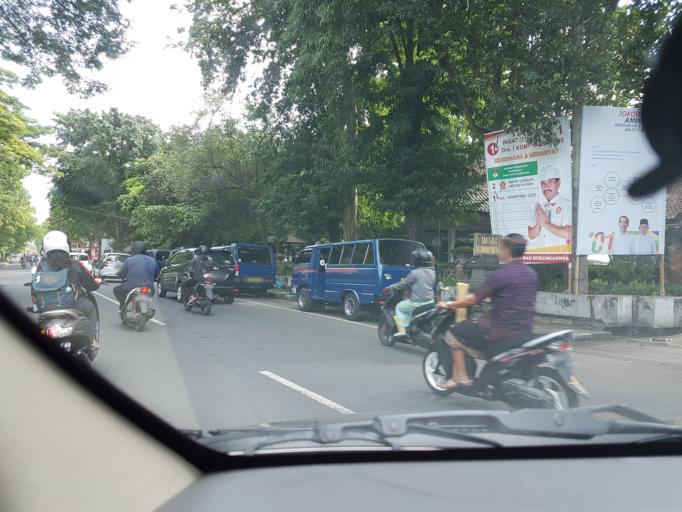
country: ID
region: Bali
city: Denpasar
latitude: -8.6625
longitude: 115.2083
